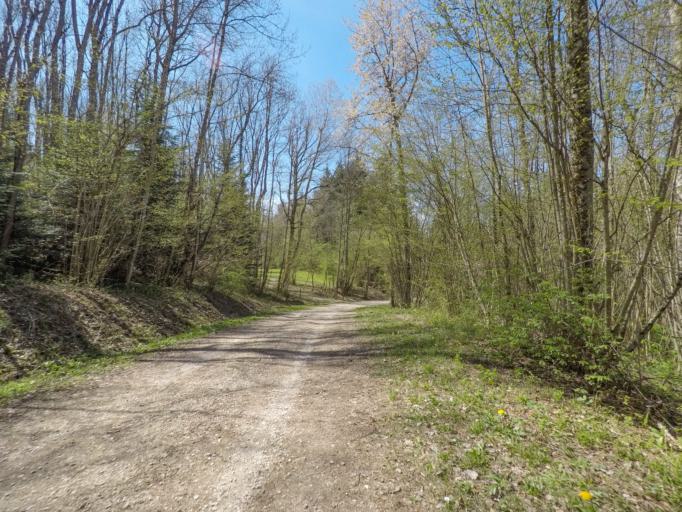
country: FR
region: Rhone-Alpes
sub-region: Departement de la Haute-Savoie
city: Archamps
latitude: 46.1173
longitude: 6.1453
